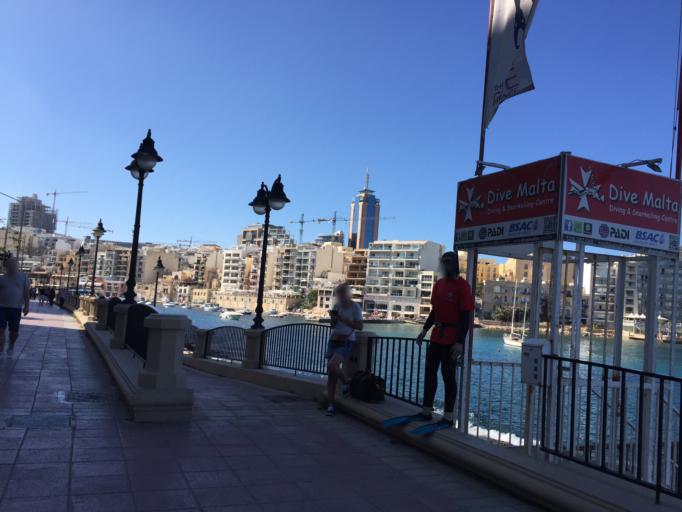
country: MT
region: Saint Julian
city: San Giljan
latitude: 35.9172
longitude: 14.4934
